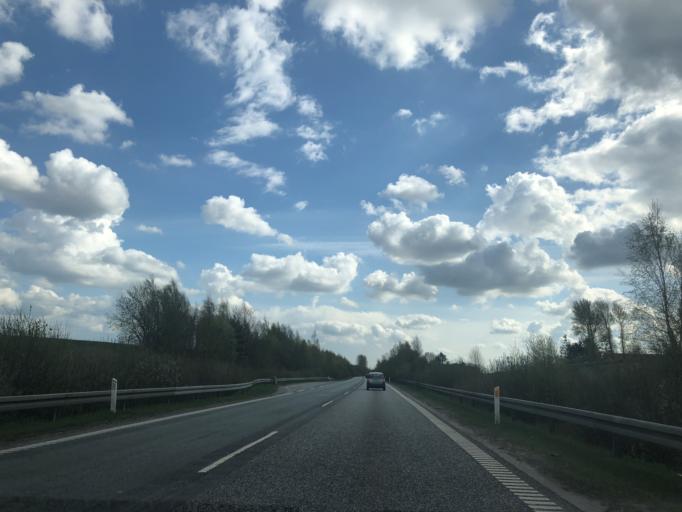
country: DK
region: Capital Region
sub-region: Gribskov Kommune
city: Helsinge
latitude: 55.9827
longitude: 12.2445
